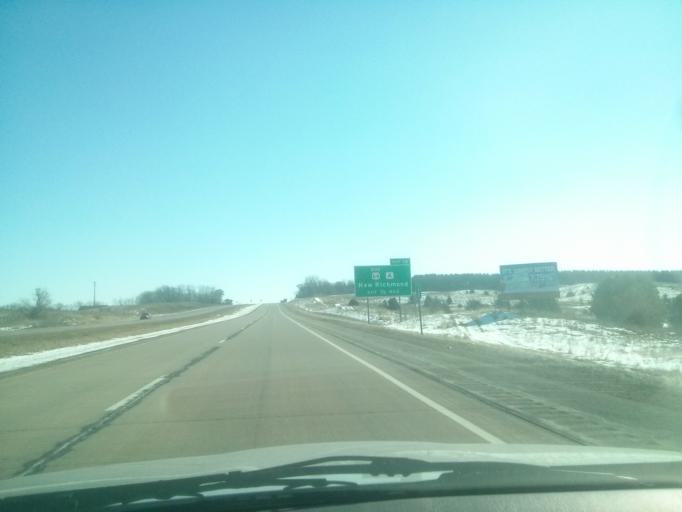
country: US
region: Wisconsin
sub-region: Saint Croix County
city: Somerset
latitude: 45.1226
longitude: -92.6066
